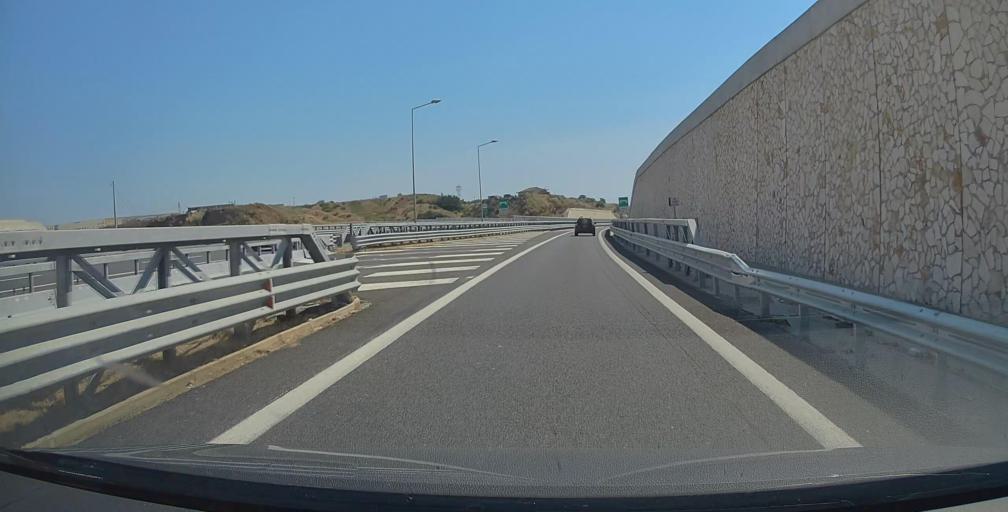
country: IT
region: Calabria
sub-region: Provincia di Reggio Calabria
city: Campo Calabro
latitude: 38.2144
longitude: 15.6471
